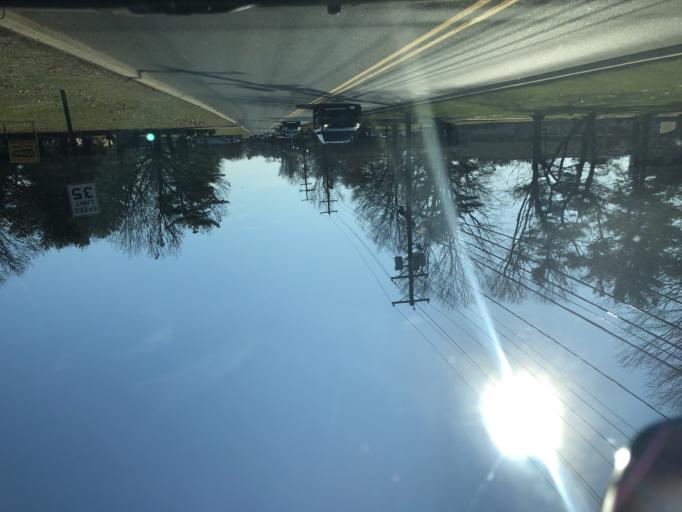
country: US
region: New Jersey
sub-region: Burlington County
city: Moorestown-Lenola
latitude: 39.9691
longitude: -74.9697
